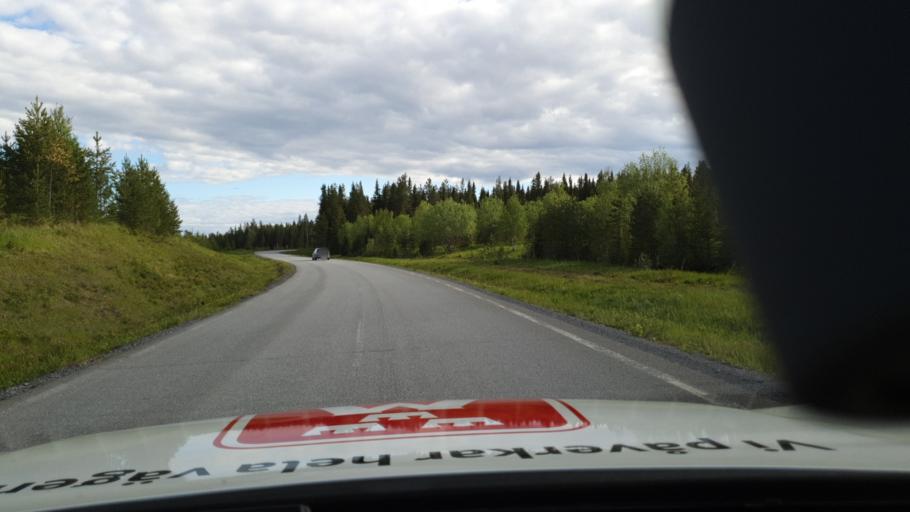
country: SE
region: Jaemtland
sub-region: Krokoms Kommun
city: Krokom
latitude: 63.2619
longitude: 14.4338
